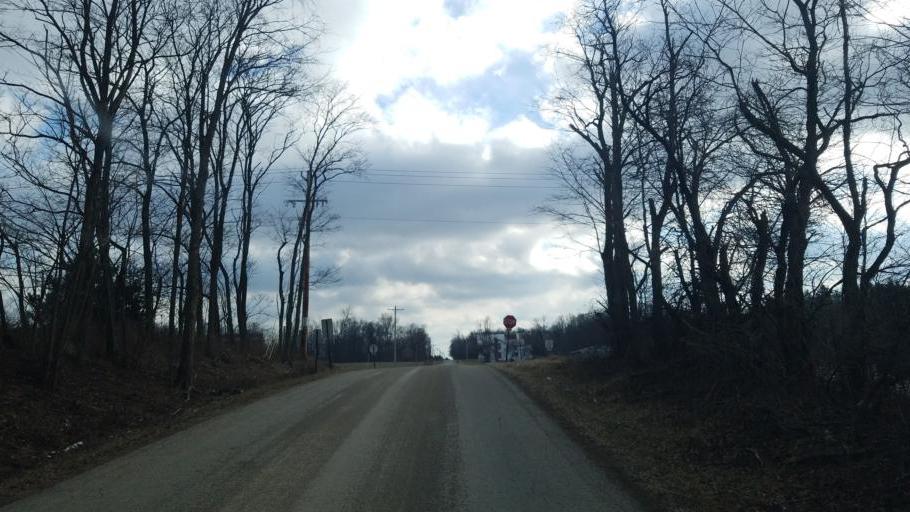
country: US
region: Ohio
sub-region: Crawford County
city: Galion
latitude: 40.6397
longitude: -82.7469
